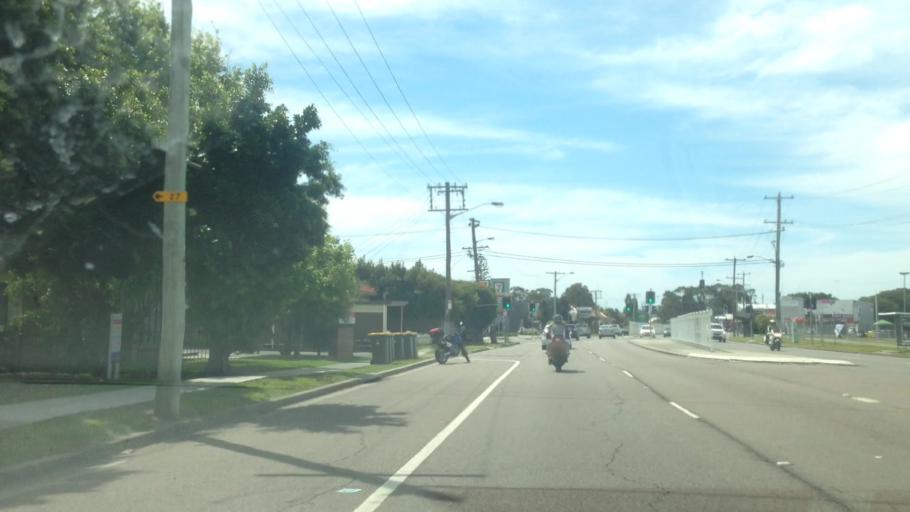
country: AU
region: New South Wales
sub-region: Newcastle
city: Broadmeadow
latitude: -32.9190
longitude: 151.7242
